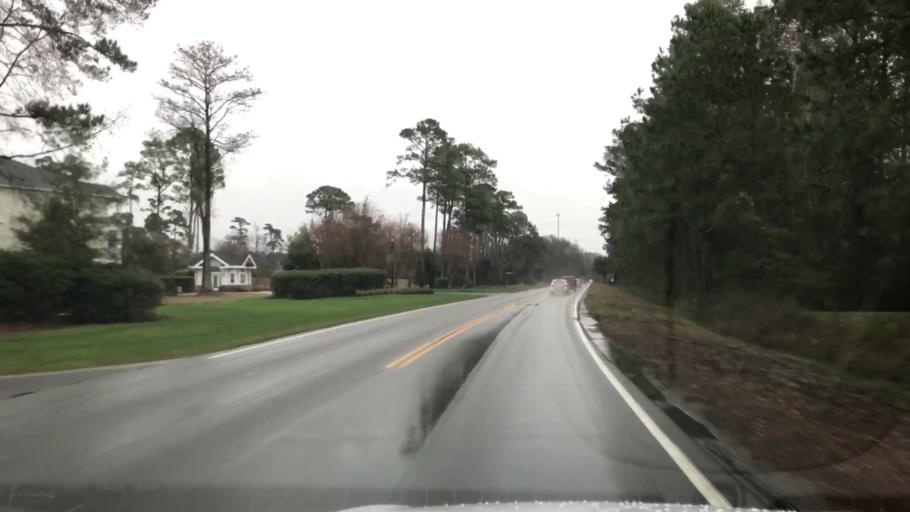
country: US
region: South Carolina
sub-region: Horry County
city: Myrtle Beach
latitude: 33.7312
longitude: -78.9074
